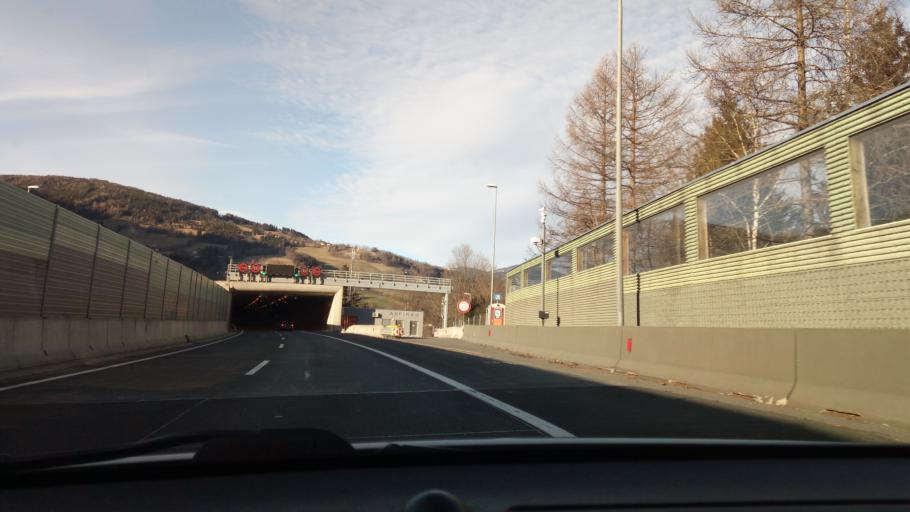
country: AT
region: Carinthia
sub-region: Politischer Bezirk Spittal an der Drau
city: Trebesing
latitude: 46.8790
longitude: 13.5109
